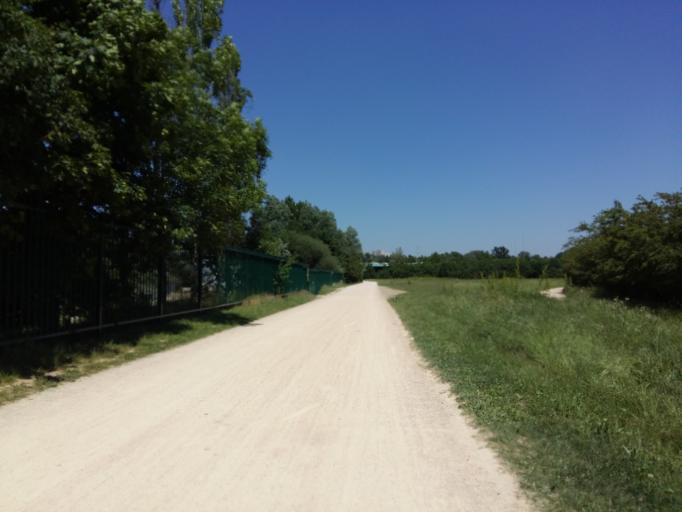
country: FR
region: Rhone-Alpes
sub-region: Departement du Rhone
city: Villeurbanne
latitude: 45.7906
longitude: 4.8791
